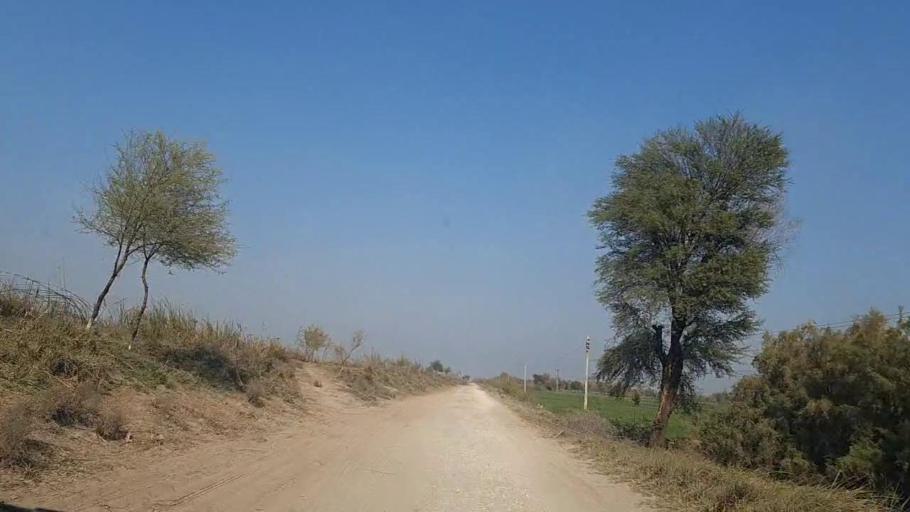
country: PK
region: Sindh
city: Sakrand
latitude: 26.0653
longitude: 68.3495
